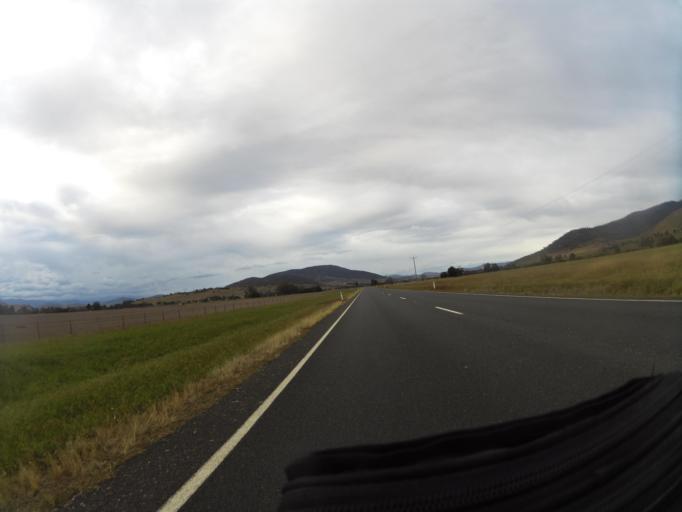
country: AU
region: New South Wales
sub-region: Snowy River
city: Jindabyne
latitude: -36.1065
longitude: 147.9801
